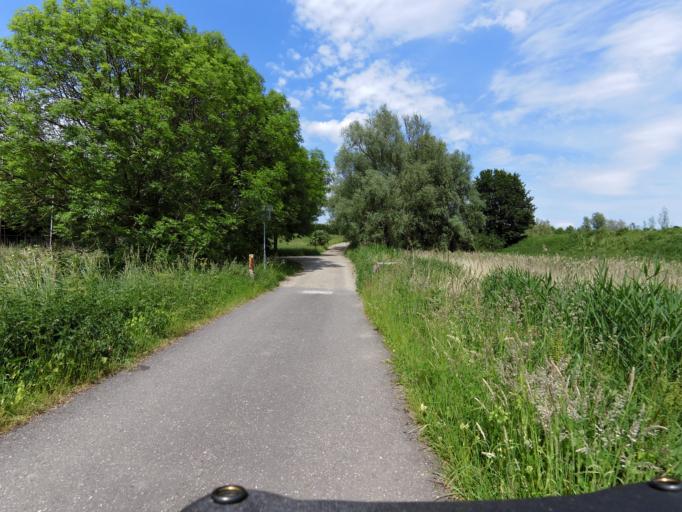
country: NL
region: North Brabant
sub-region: Gemeente Woudrichem
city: Woudrichem
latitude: 51.8108
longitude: 5.0608
